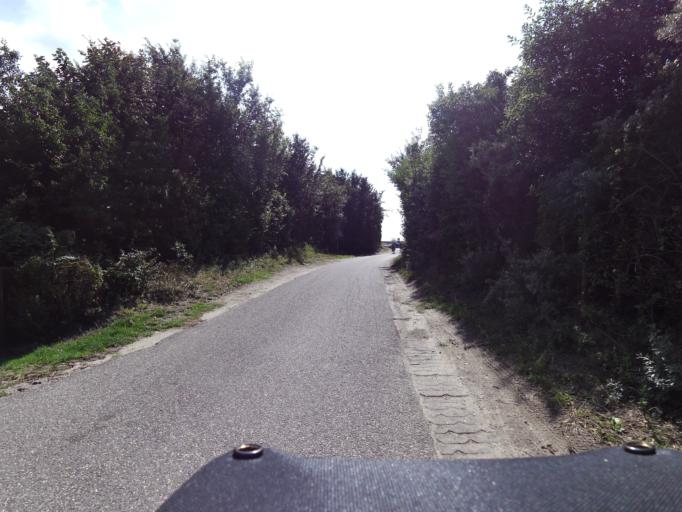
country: NL
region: South Holland
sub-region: Gemeente Goeree-Overflakkee
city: Ouddorp
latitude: 51.8117
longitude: 3.8665
